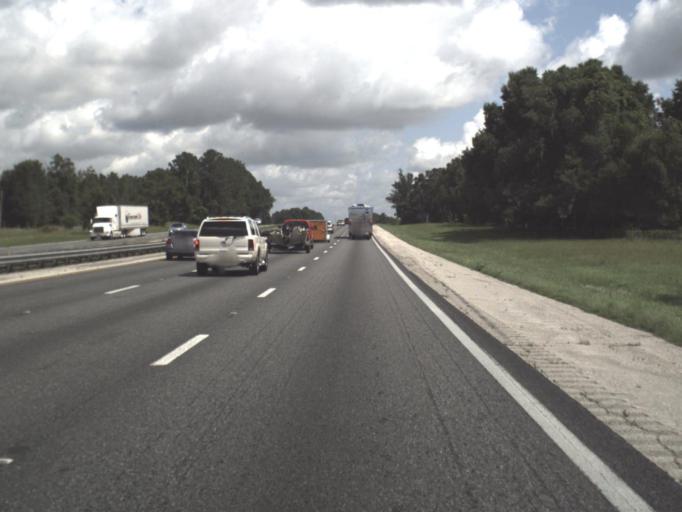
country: US
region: Florida
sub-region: Alachua County
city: High Springs
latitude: 29.9137
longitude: -82.5529
